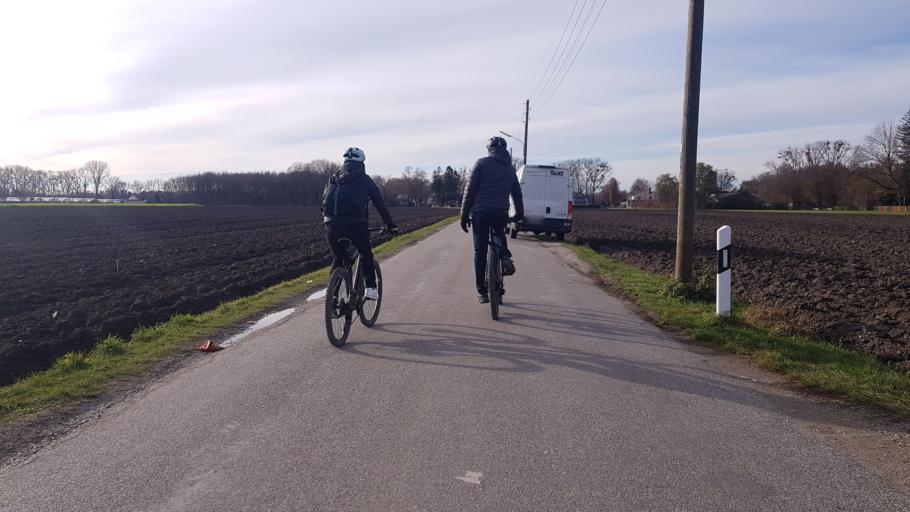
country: DE
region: Bavaria
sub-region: Upper Bavaria
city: Oberschleissheim
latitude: 48.2148
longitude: 11.5270
